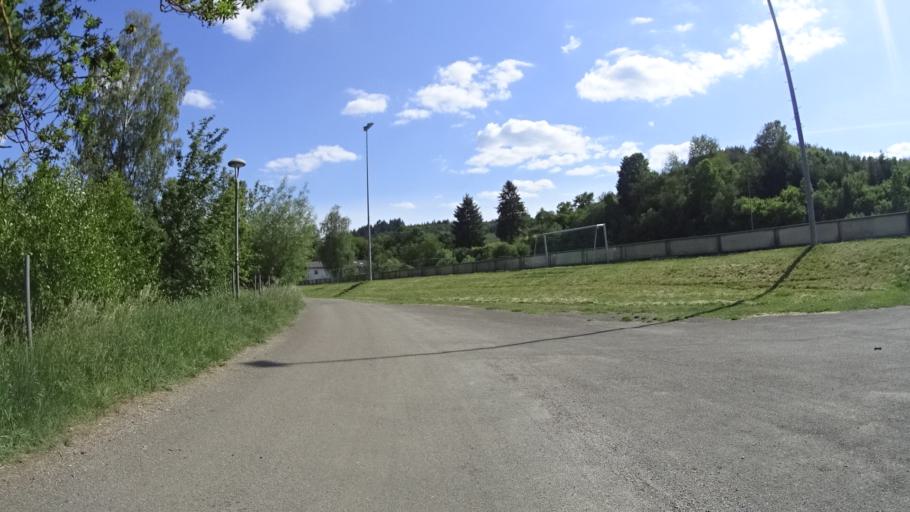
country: DE
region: Baden-Wuerttemberg
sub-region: Karlsruhe Region
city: Hardheim
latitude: 49.5778
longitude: 9.4859
